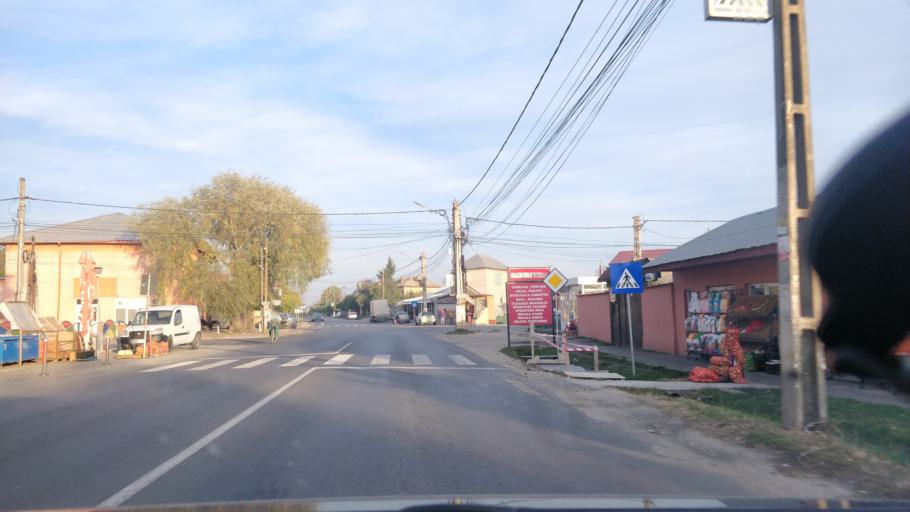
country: RO
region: Ilfov
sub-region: Comuna Ciorogarla
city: Ciorogarla
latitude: 44.4435
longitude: 25.8833
